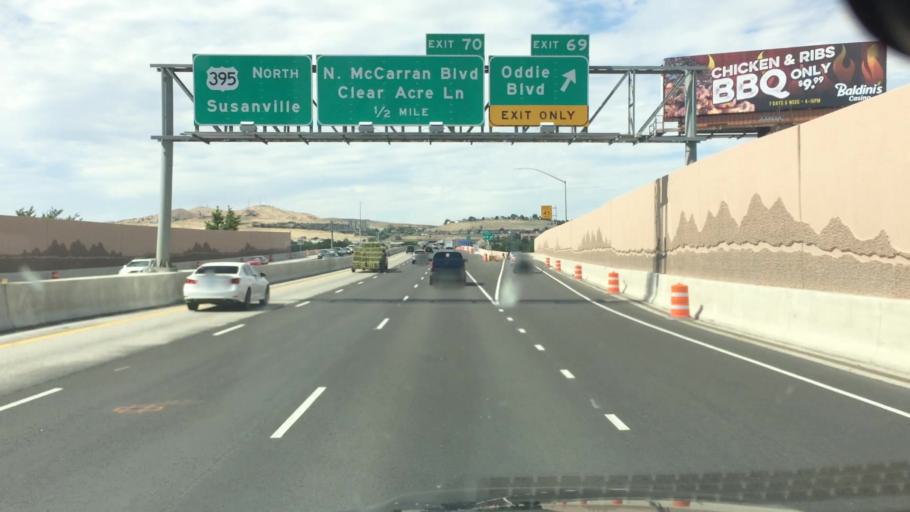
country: US
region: Nevada
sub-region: Washoe County
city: Reno
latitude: 39.5425
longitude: -119.7878
